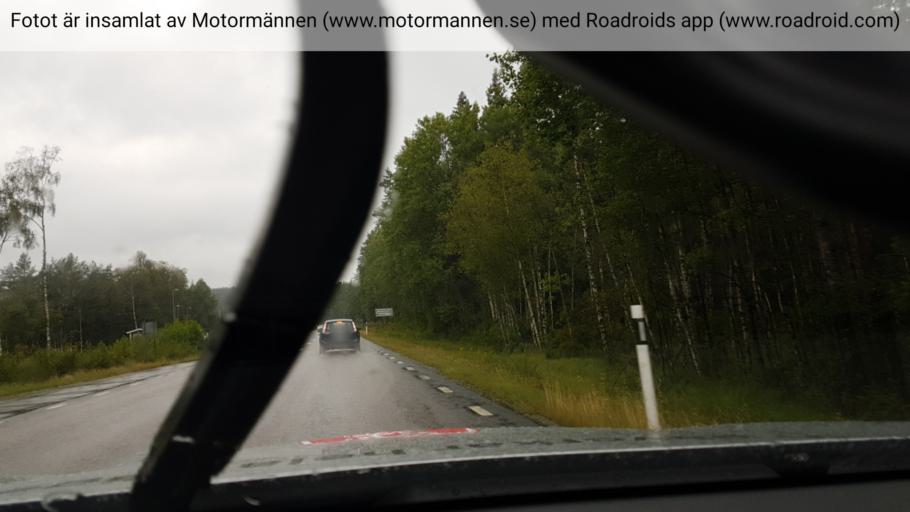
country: SE
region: Vaestra Goetaland
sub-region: Dals-Ed Kommun
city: Ed
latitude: 58.8772
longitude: 11.8304
